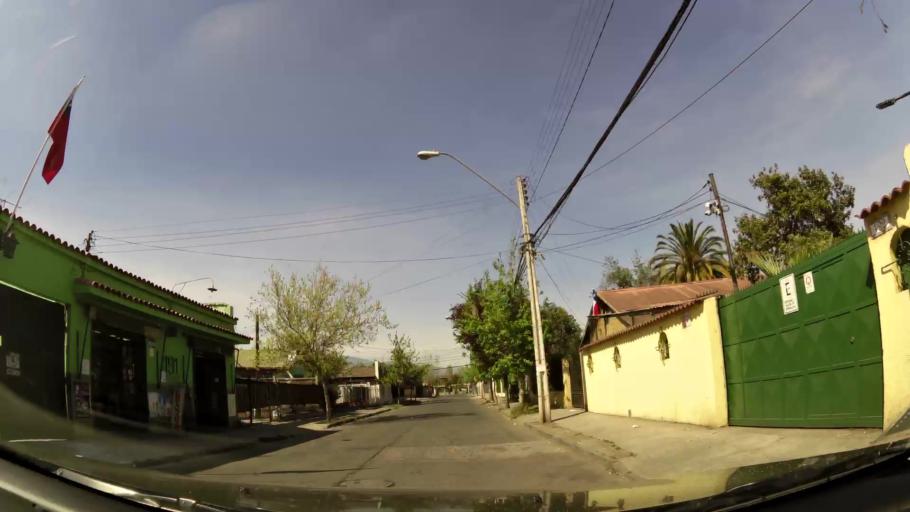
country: CL
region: Santiago Metropolitan
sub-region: Provincia de Cordillera
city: Puente Alto
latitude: -33.6109
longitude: -70.5818
